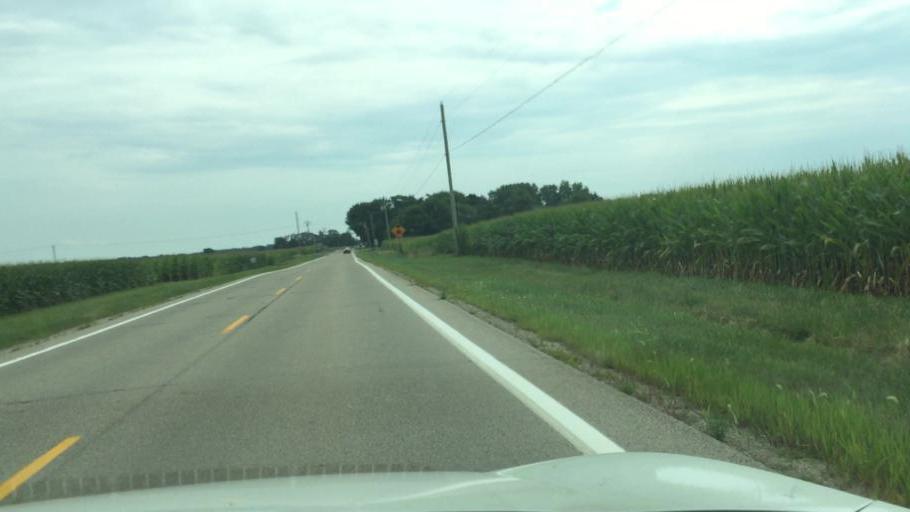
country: US
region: Ohio
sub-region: Champaign County
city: Mechanicsburg
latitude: 40.1454
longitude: -83.5293
